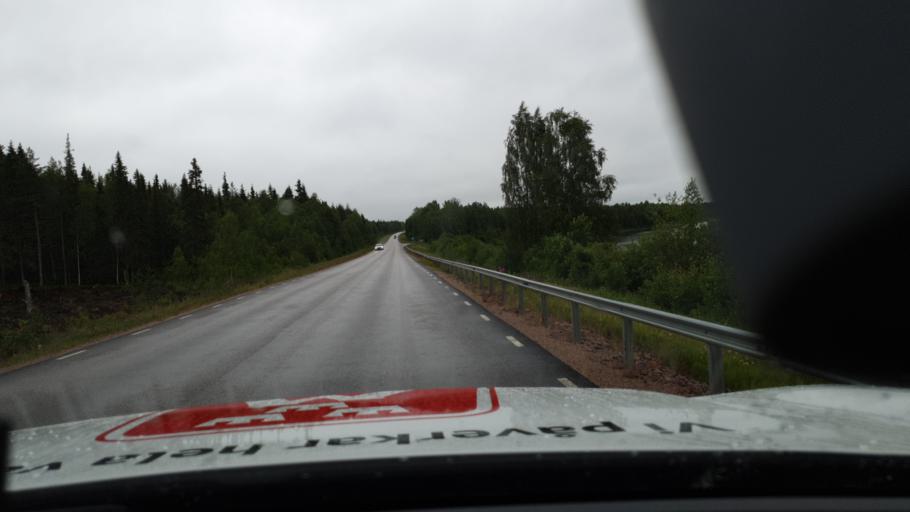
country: SE
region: Norrbotten
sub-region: Overtornea Kommun
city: OEvertornea
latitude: 66.4917
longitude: 23.7098
